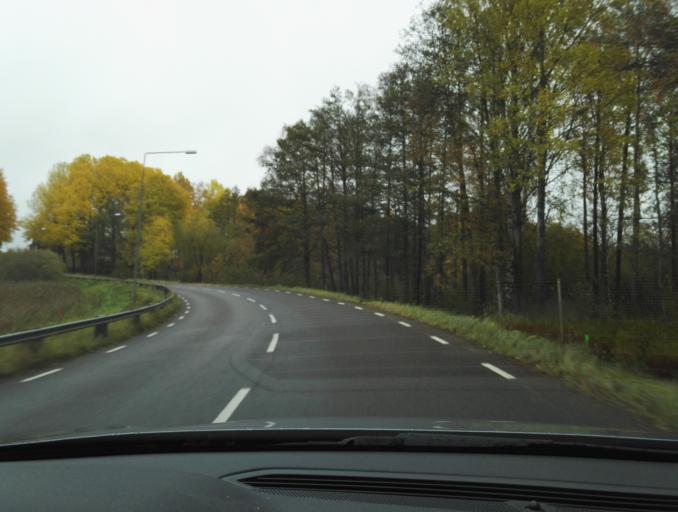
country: SE
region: Kronoberg
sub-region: Vaxjo Kommun
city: Rottne
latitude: 57.0251
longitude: 14.8775
